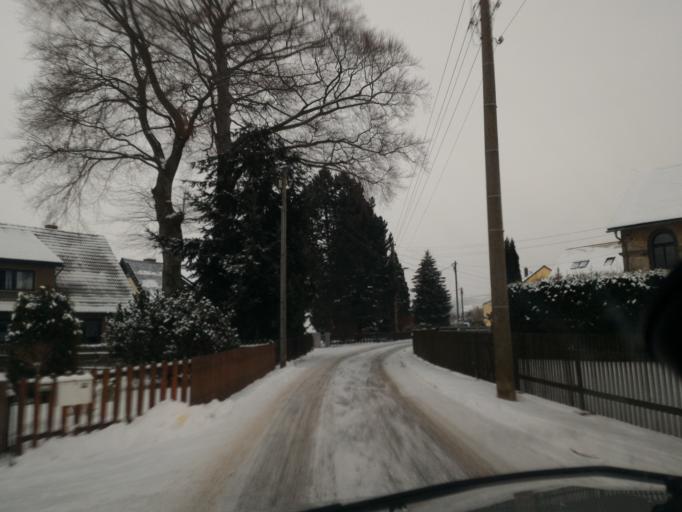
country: DE
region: Saxony
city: Seifhennersdorf
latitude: 50.9337
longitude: 14.6005
